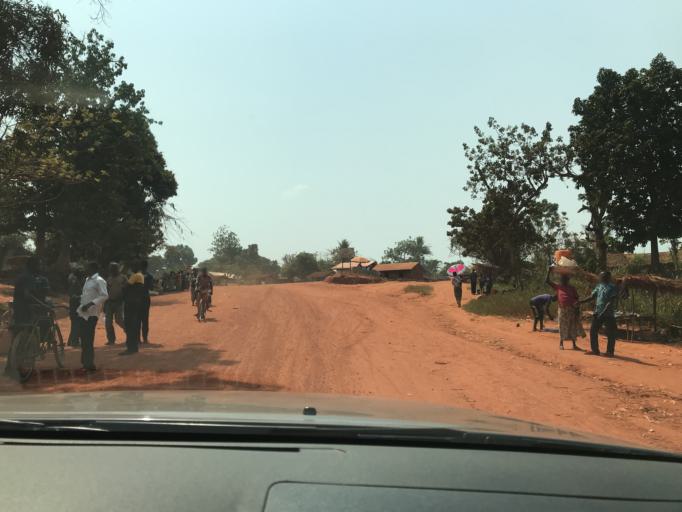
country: CD
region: Equateur
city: Gemena
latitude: 3.2237
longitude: 19.7758
